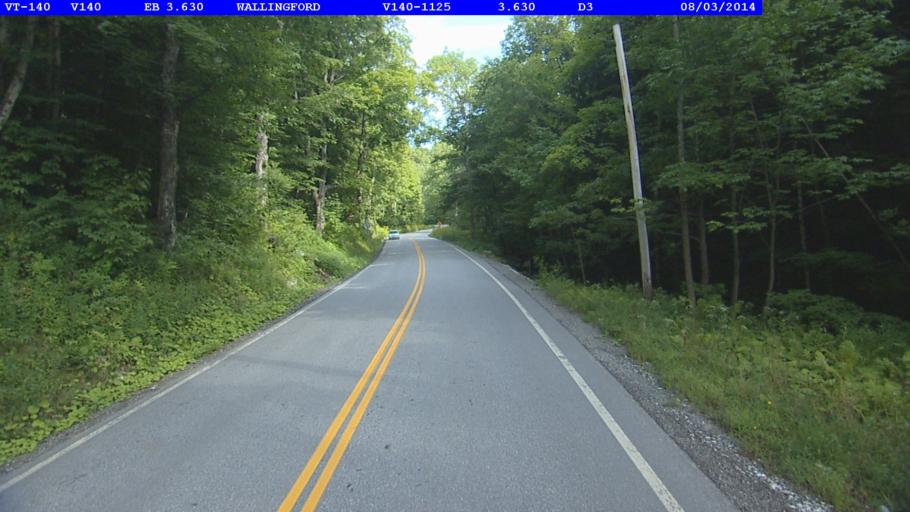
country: US
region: Vermont
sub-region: Rutland County
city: Rutland
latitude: 43.4599
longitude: -72.9170
